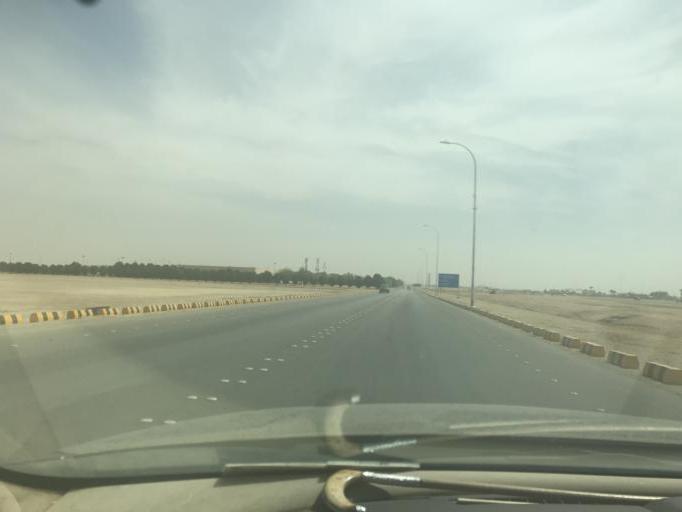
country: SA
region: Ar Riyad
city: Riyadh
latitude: 24.9831
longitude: 46.6836
